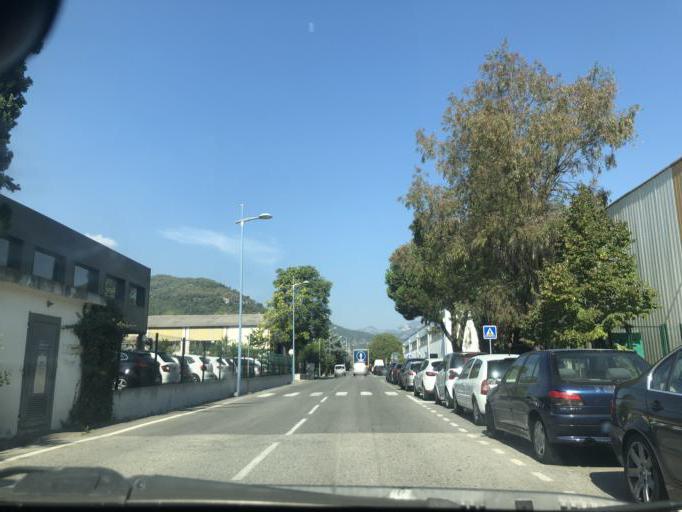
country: FR
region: Provence-Alpes-Cote d'Azur
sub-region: Departement des Alpes-Maritimes
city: Carros
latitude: 43.7905
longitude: 7.2059
